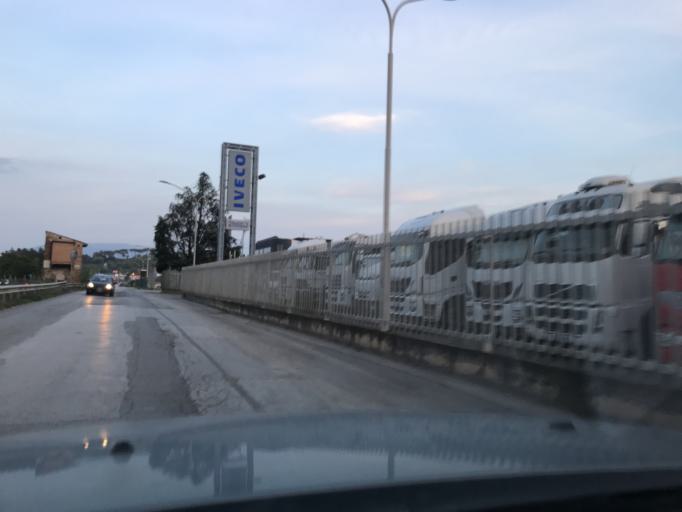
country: IT
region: Umbria
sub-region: Provincia di Perugia
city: Via Lippia
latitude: 43.0888
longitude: 12.4575
